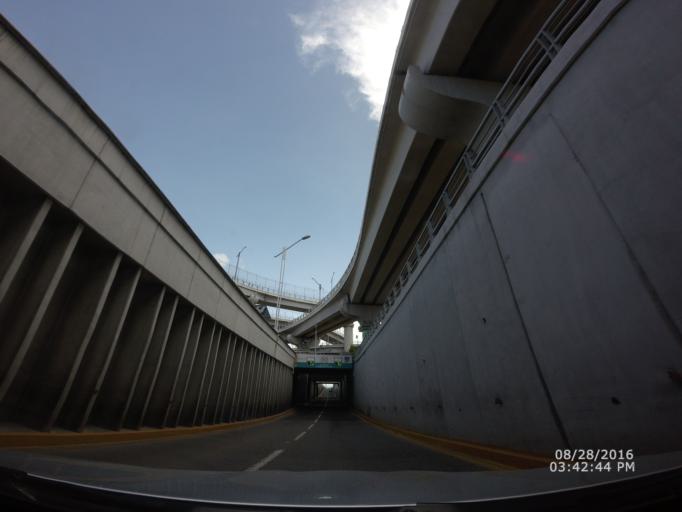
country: MX
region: Hidalgo
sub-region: Mineral de la Reforma
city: PRI Chacon
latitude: 20.0904
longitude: -98.7495
